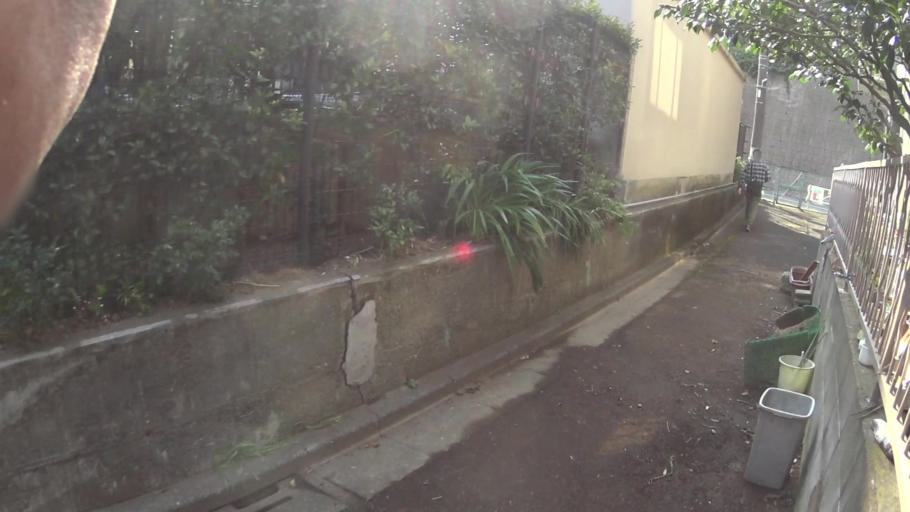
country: JP
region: Tokyo
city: Tokyo
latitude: 35.6408
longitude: 139.7155
